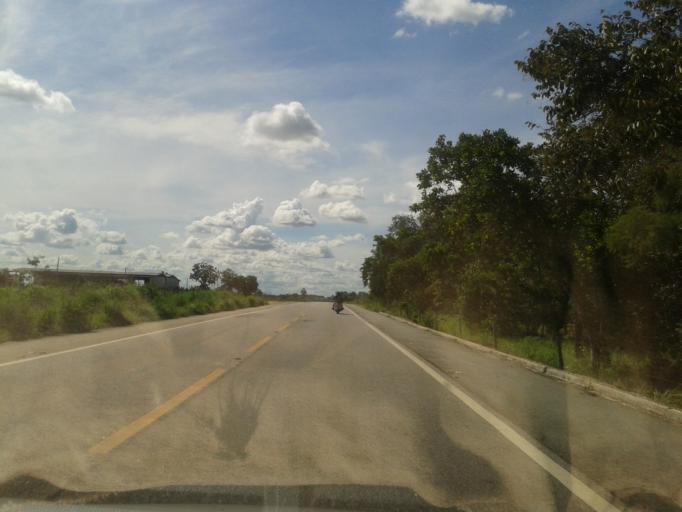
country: BR
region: Goias
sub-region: Itapirapua
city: Itapirapua
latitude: -15.2976
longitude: -50.4580
